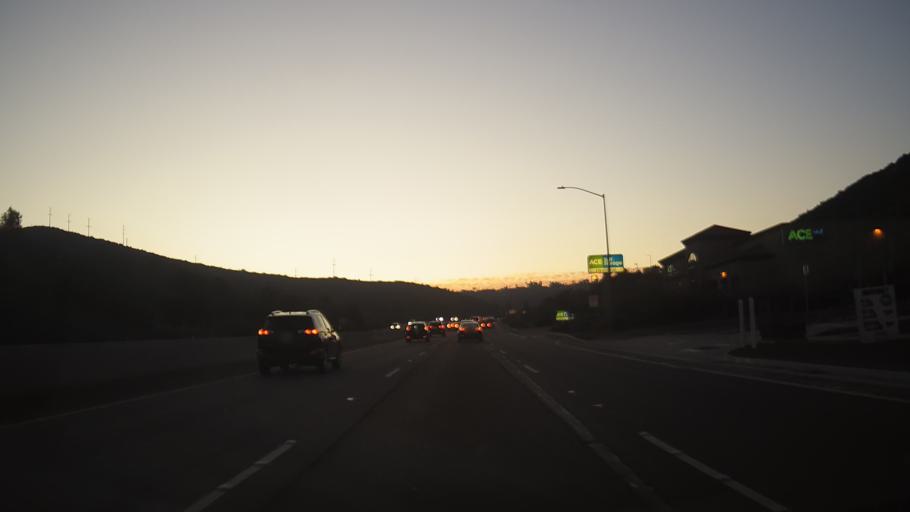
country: US
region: California
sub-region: San Diego County
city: Rancho San Diego
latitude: 32.7402
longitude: -116.9436
